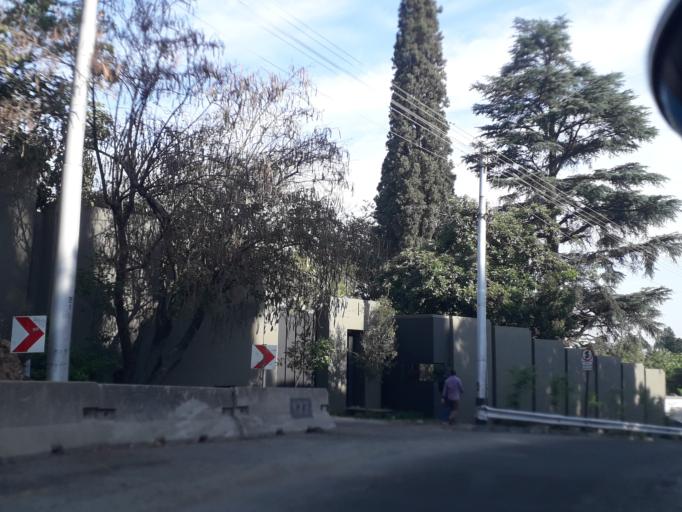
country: ZA
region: Gauteng
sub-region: City of Johannesburg Metropolitan Municipality
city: Johannesburg
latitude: -26.1771
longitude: 28.0197
